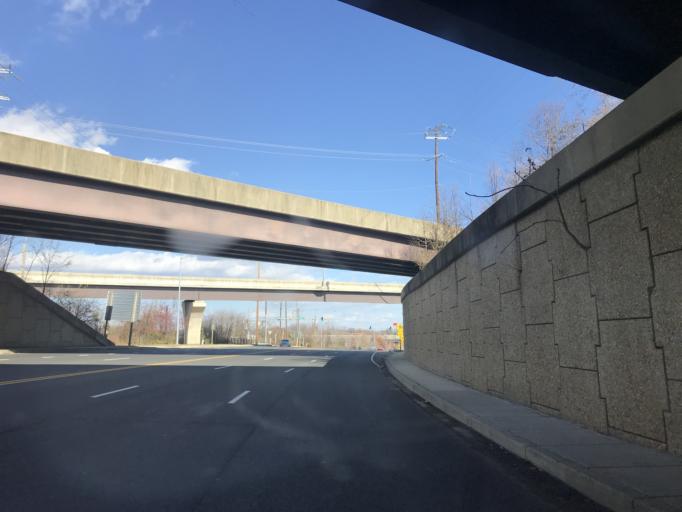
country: US
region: Maryland
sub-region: Prince George's County
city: Forest Heights
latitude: 38.8003
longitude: -77.0019
